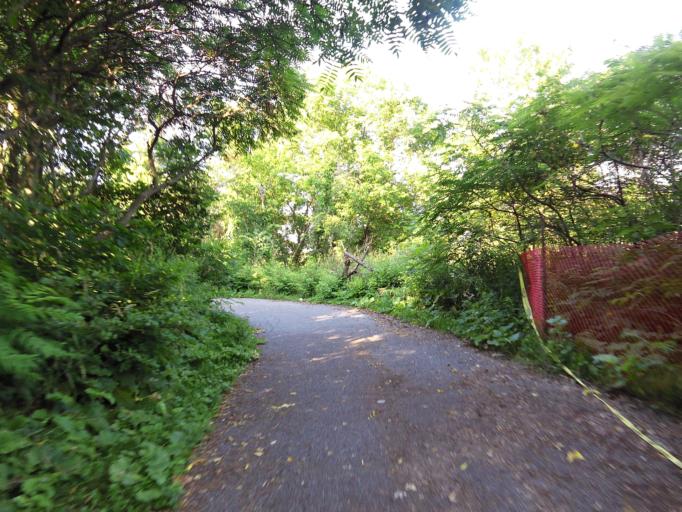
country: CA
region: Ontario
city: Ottawa
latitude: 45.3451
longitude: -75.7196
